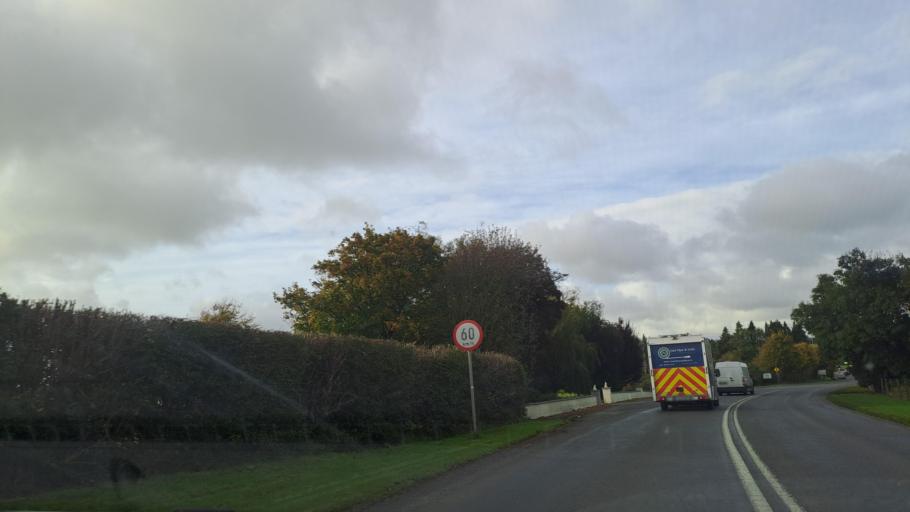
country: IE
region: Ulster
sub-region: An Cabhan
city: Kingscourt
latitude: 53.8129
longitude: -6.7396
